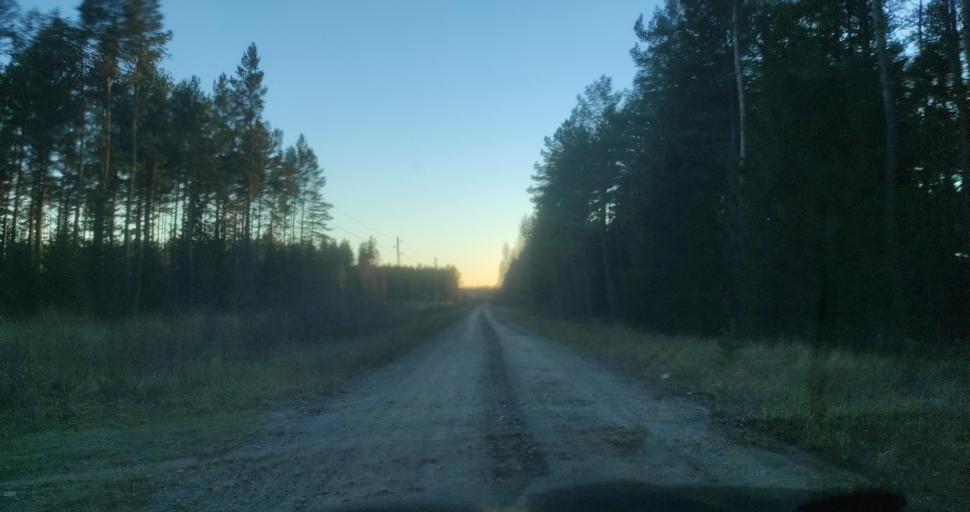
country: LV
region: Dundaga
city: Dundaga
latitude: 57.3728
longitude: 22.0775
